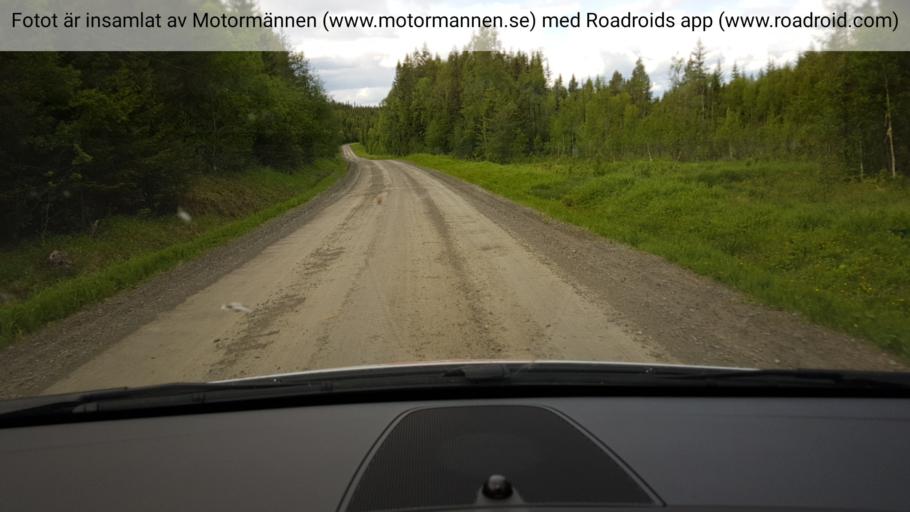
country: SE
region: Jaemtland
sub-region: Bergs Kommun
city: Hoverberg
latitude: 62.9899
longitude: 14.1718
